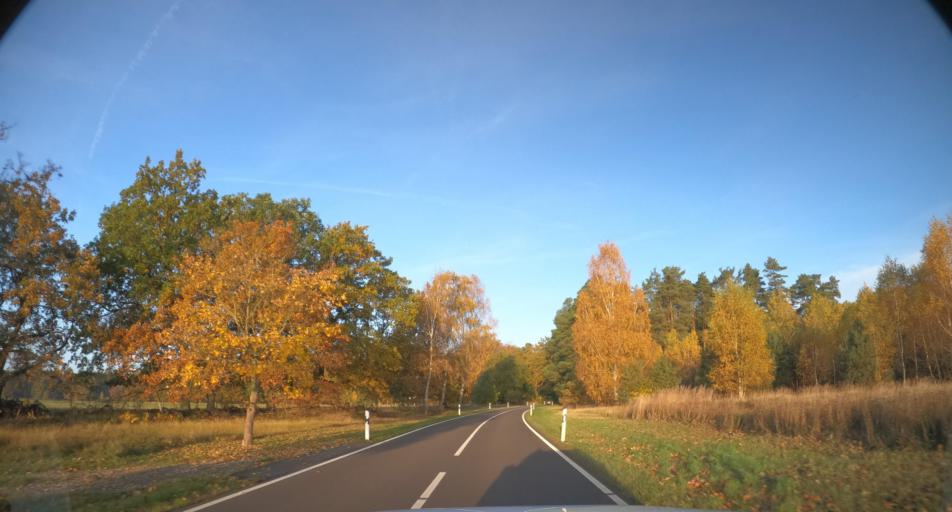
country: DE
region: Mecklenburg-Vorpommern
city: Ahlbeck
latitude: 53.6476
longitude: 14.1936
